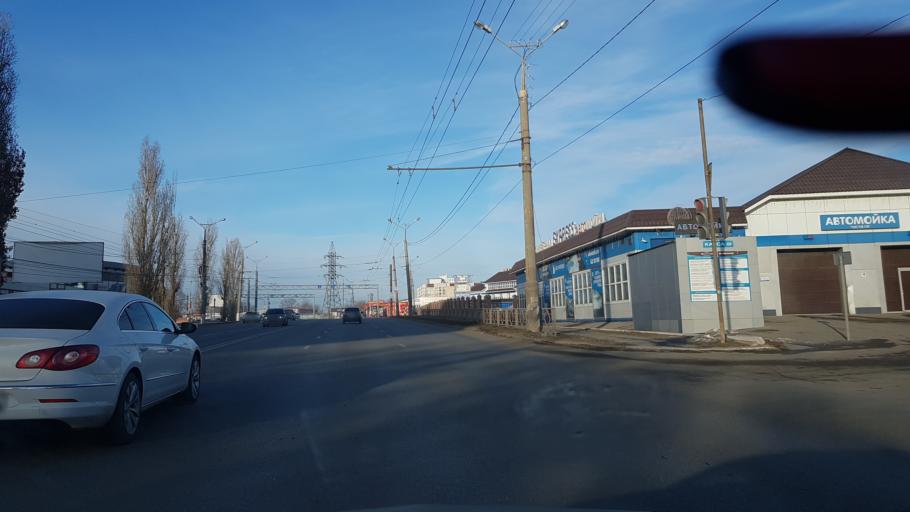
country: RU
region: Samara
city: Tol'yatti
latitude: 53.5336
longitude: 49.3958
